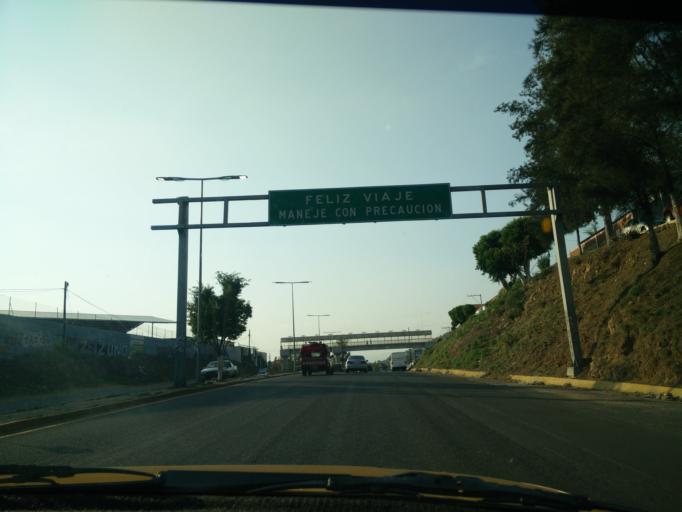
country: MX
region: Oaxaca
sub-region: Santa Maria Atzompa
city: San Jeronimo Yahuiche
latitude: 17.0962
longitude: -96.7494
